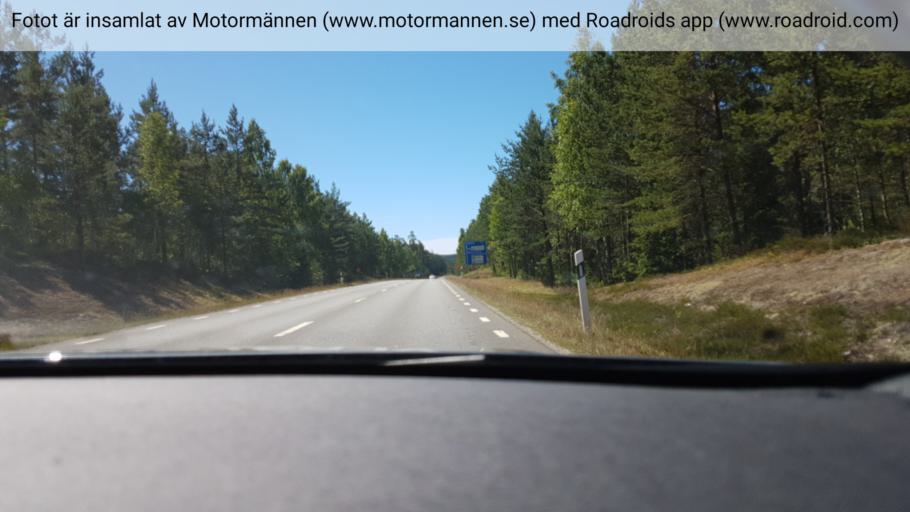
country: SE
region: Joenkoeping
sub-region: Mullsjo Kommun
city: Mullsjoe
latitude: 57.7738
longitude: 13.8345
